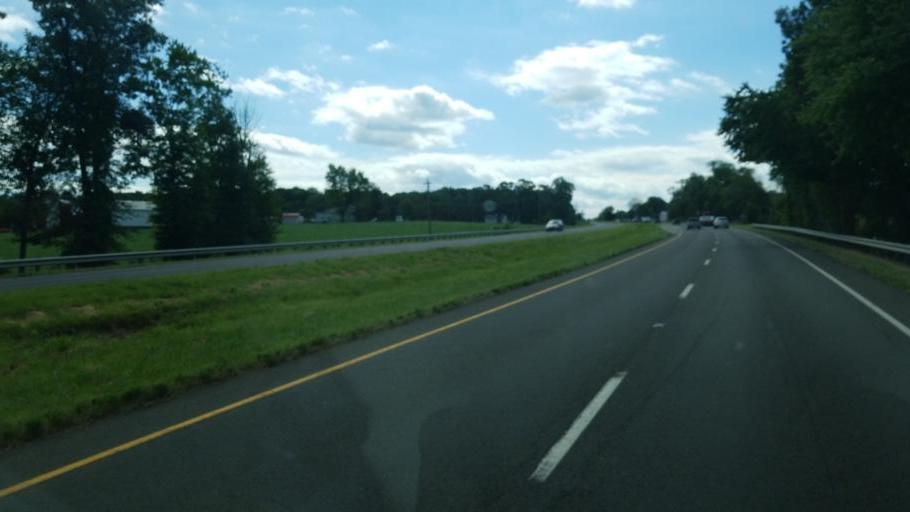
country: US
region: Virginia
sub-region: Fauquier County
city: Bealeton
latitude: 38.5117
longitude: -77.7151
